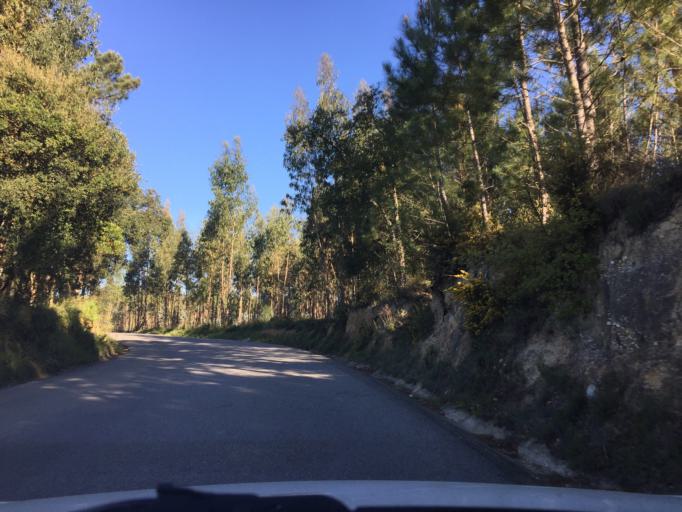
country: PT
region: Aveiro
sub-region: Anadia
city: Sangalhos
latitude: 40.4548
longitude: -8.4857
